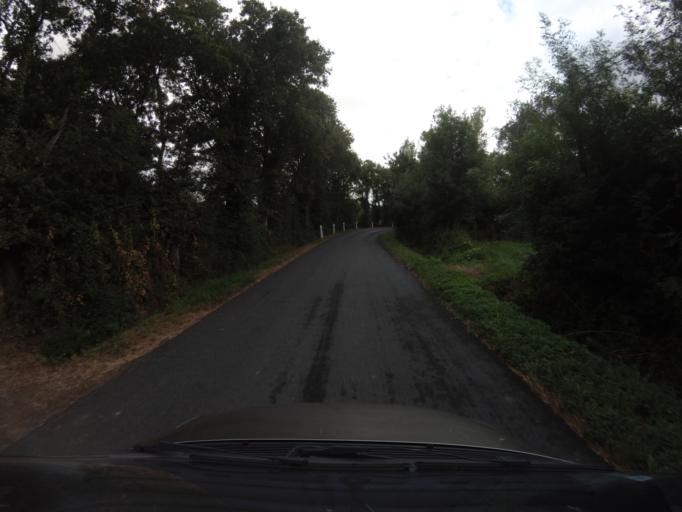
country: FR
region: Pays de la Loire
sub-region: Departement de la Vendee
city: La Bernardiere
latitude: 47.0353
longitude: -1.2864
